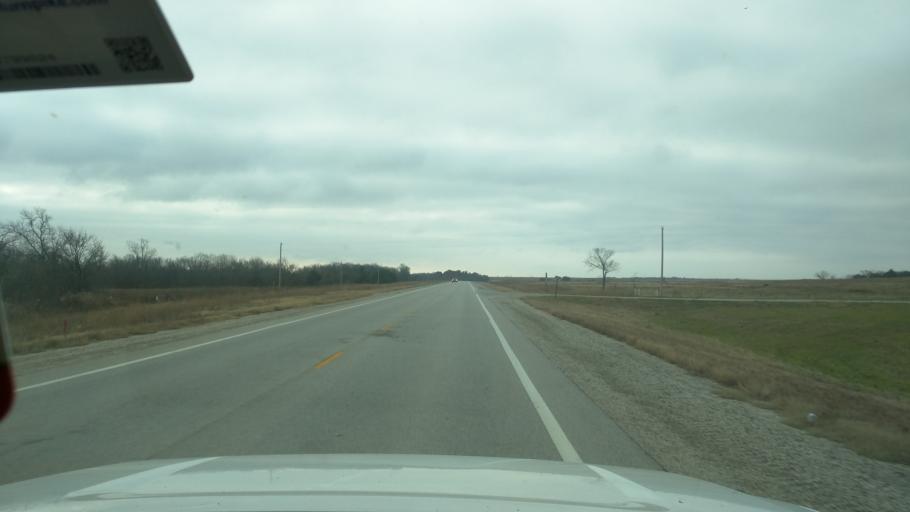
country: US
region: Kansas
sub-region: Elk County
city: Howard
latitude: 37.5489
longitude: -96.2533
